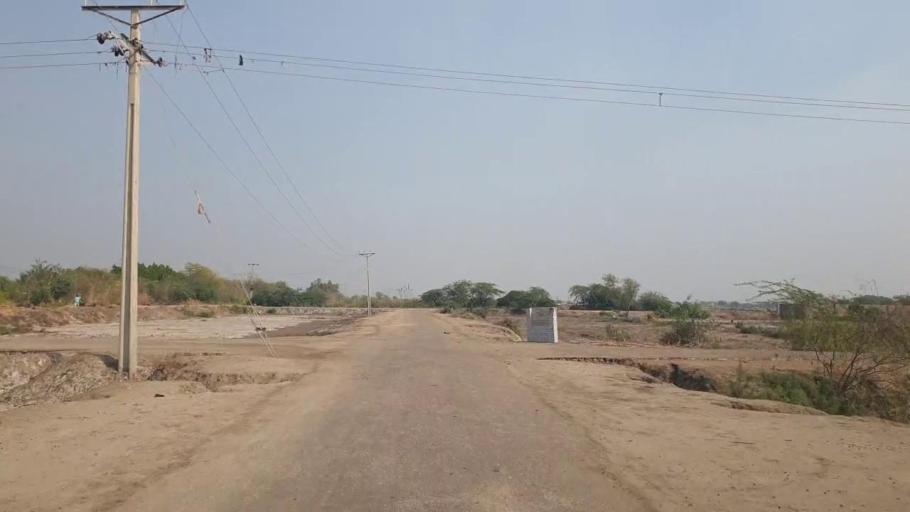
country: PK
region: Sindh
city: Jamshoro
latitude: 25.4592
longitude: 68.3351
